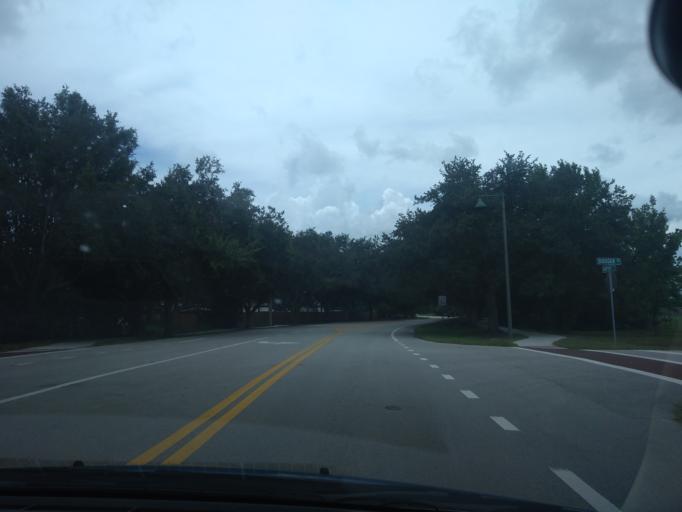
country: US
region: Florida
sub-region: Indian River County
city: Vero Beach
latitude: 27.6460
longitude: -80.4198
